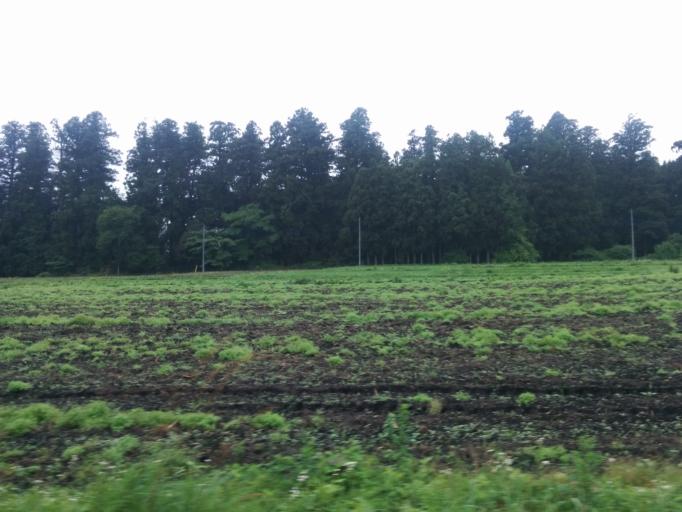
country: JP
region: Tochigi
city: Imaichi
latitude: 36.6452
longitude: 139.7251
